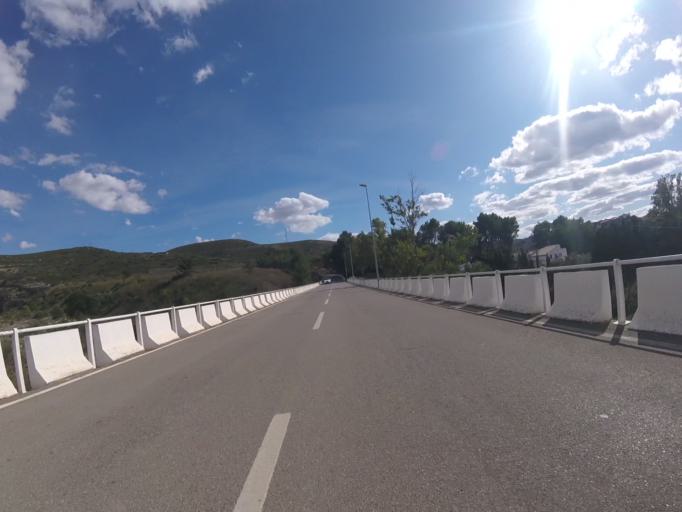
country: ES
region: Valencia
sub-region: Provincia de Castello
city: Cuevas de Vinroma
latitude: 40.3150
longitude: 0.1237
